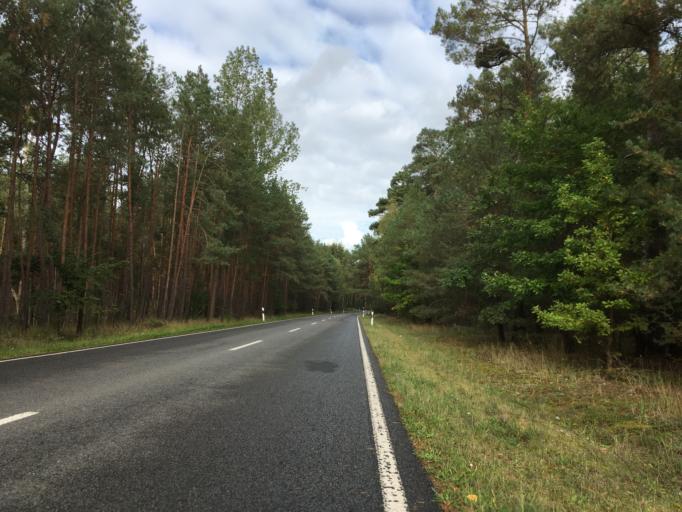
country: PL
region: West Pomeranian Voivodeship
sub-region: Powiat gryfinski
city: Cedynia
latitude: 52.9005
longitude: 14.1283
